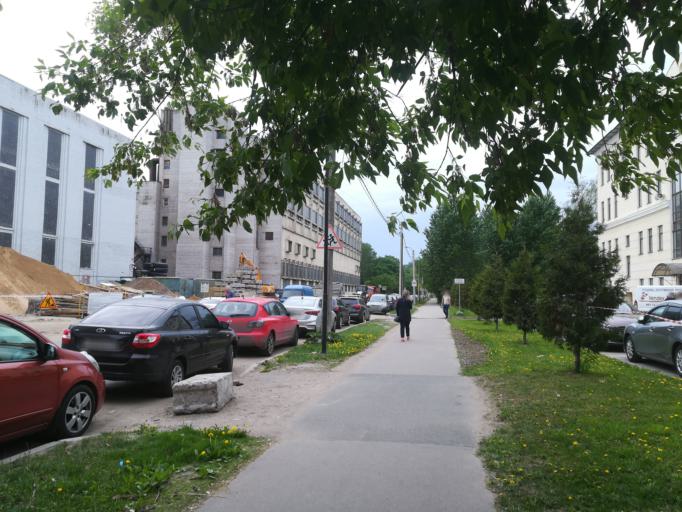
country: RU
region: St.-Petersburg
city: Vasyl'evsky Ostrov
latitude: 59.9518
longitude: 30.2632
